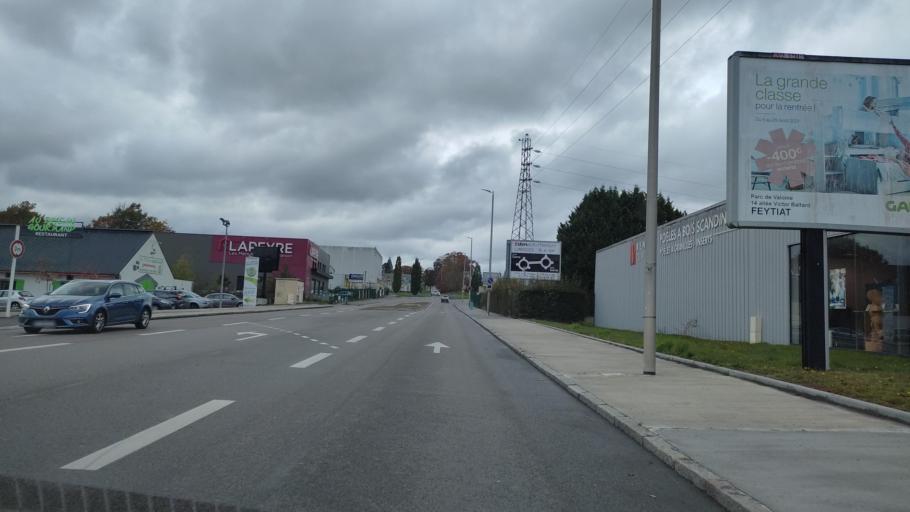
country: FR
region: Limousin
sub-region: Departement de la Haute-Vienne
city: Chaptelat
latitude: 45.8850
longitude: 1.2811
